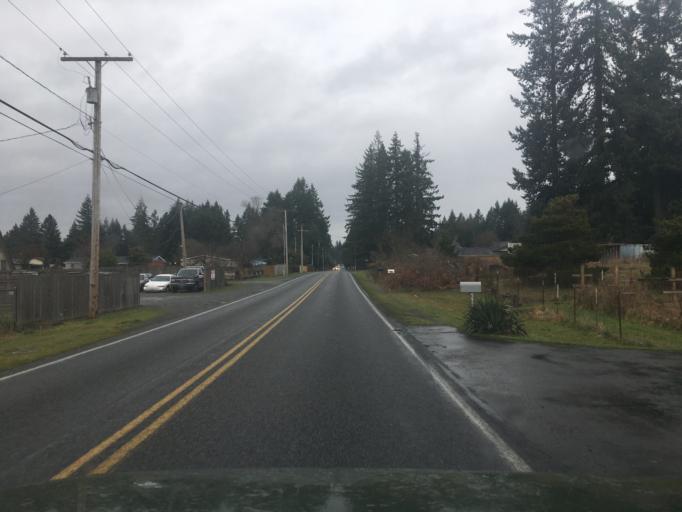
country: US
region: Washington
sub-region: Thurston County
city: Tanglewilde-Thompson Place
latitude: 47.0444
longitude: -122.7913
